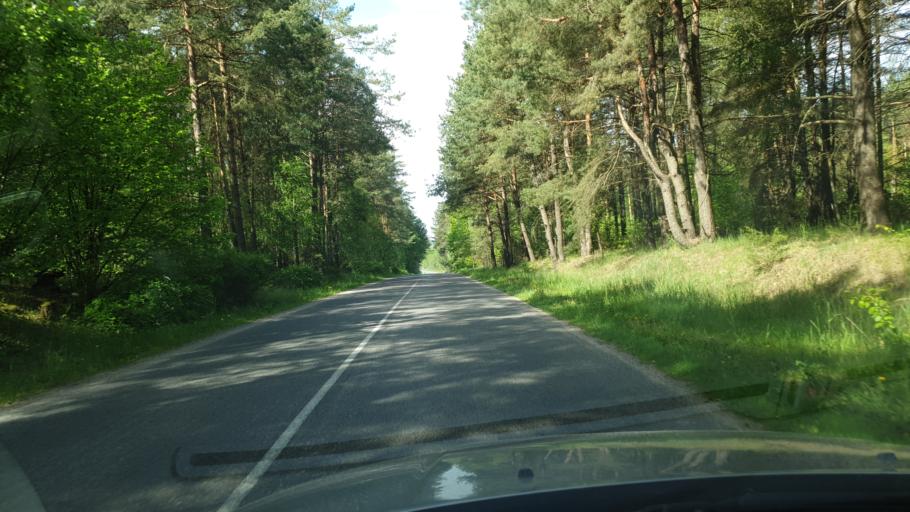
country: BY
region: Grodnenskaya
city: Mir
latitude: 53.4241
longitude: 26.3682
